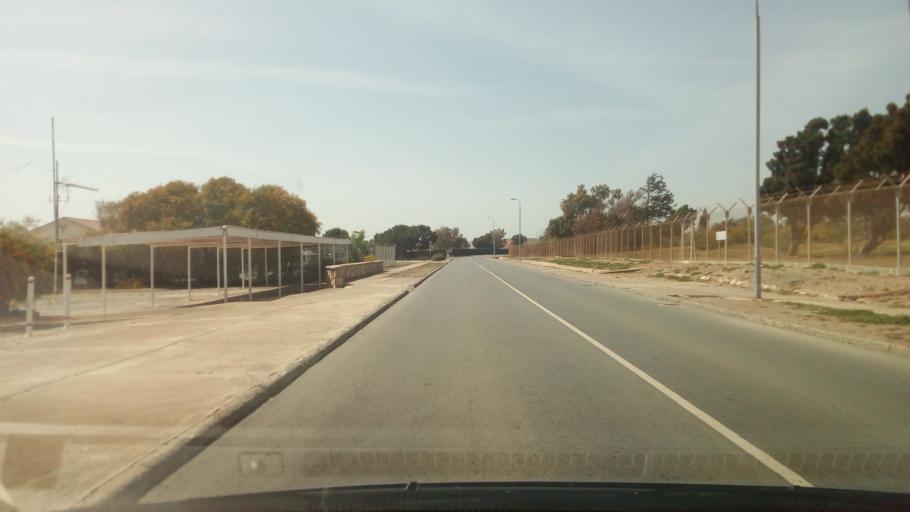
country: CY
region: Larnaka
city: Xylotymbou
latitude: 34.9818
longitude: 33.7275
